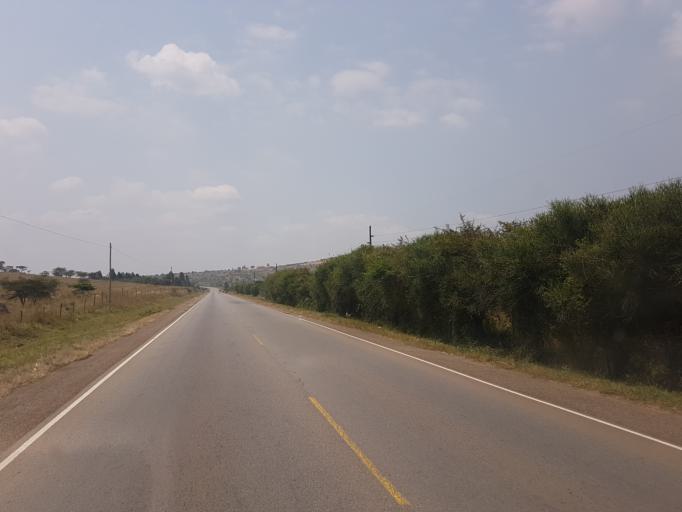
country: UG
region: Western Region
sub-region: Mbarara District
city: Mbarara
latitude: -0.5060
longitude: 30.8445
